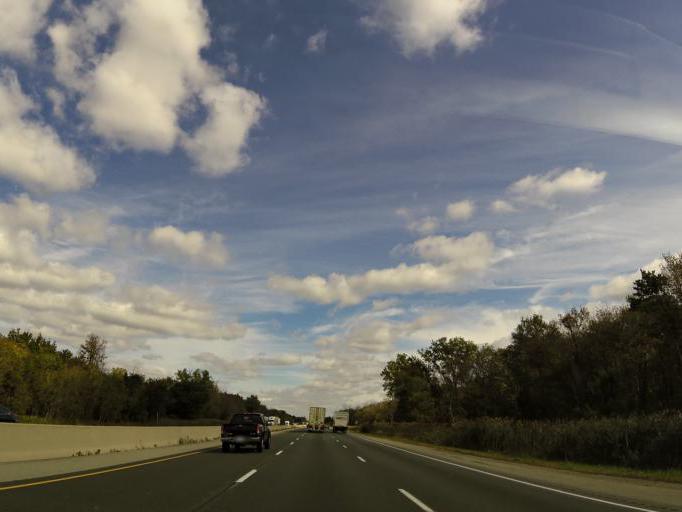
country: CA
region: Ontario
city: Dorchester
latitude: 42.9673
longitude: -81.0052
